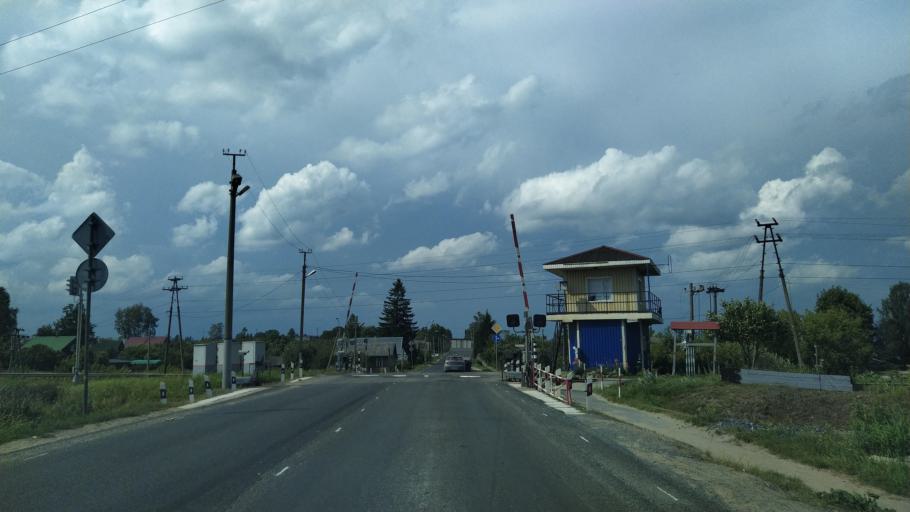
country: RU
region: Pskov
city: Porkhov
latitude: 57.7721
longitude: 29.5504
